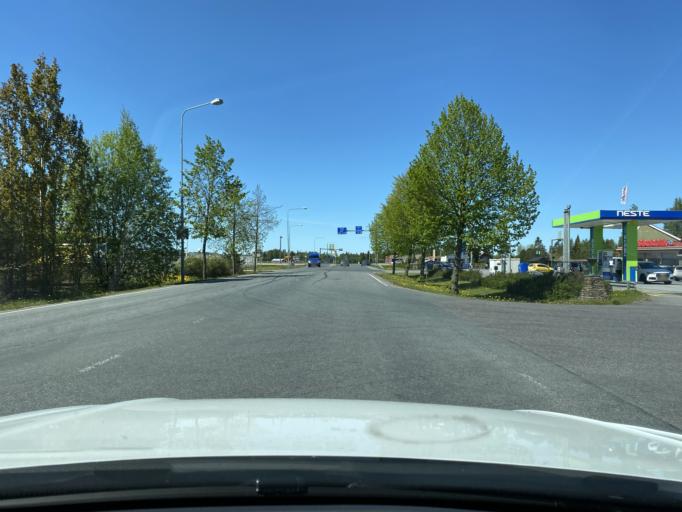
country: FI
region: Satakunta
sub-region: Pori
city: Huittinen
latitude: 61.1744
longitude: 22.6825
